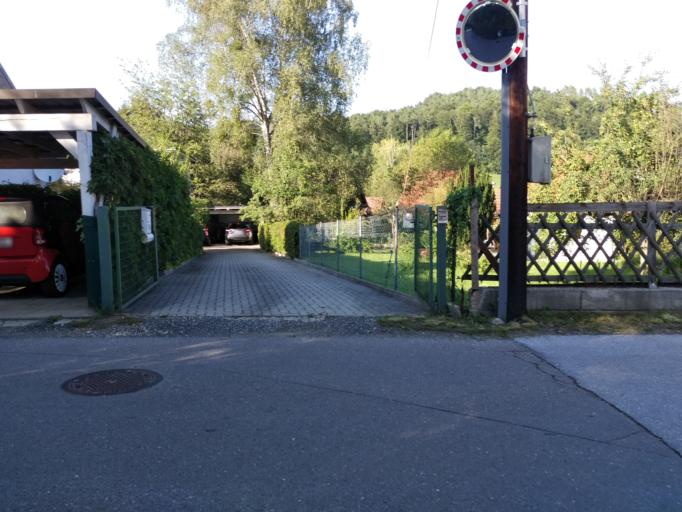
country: AT
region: Styria
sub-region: Graz Stadt
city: Mariatrost
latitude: 47.0733
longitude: 15.5010
